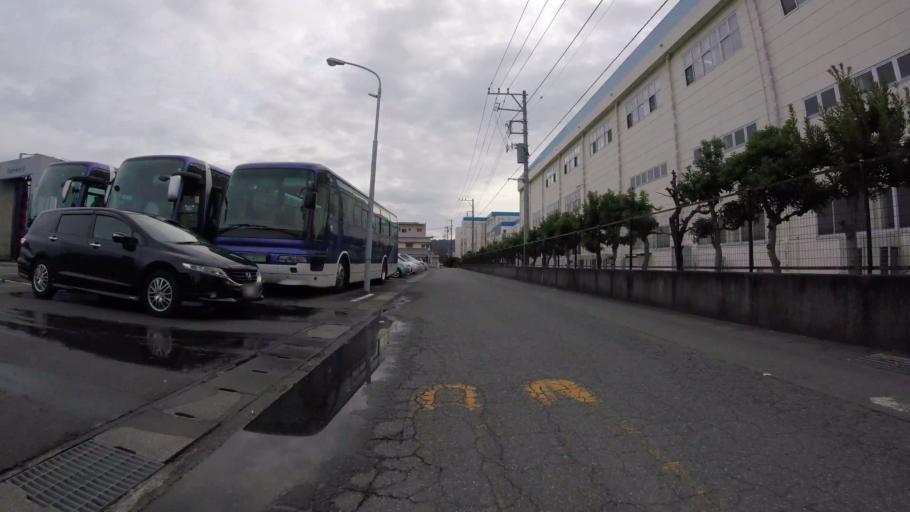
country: JP
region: Shizuoka
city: Mishima
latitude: 35.0931
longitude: 138.9104
